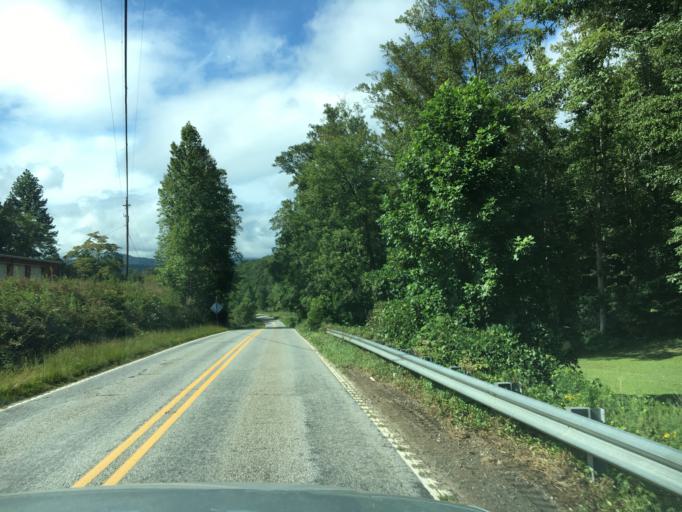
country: US
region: North Carolina
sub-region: Rutherford County
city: Lake Lure
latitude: 35.3766
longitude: -82.1883
